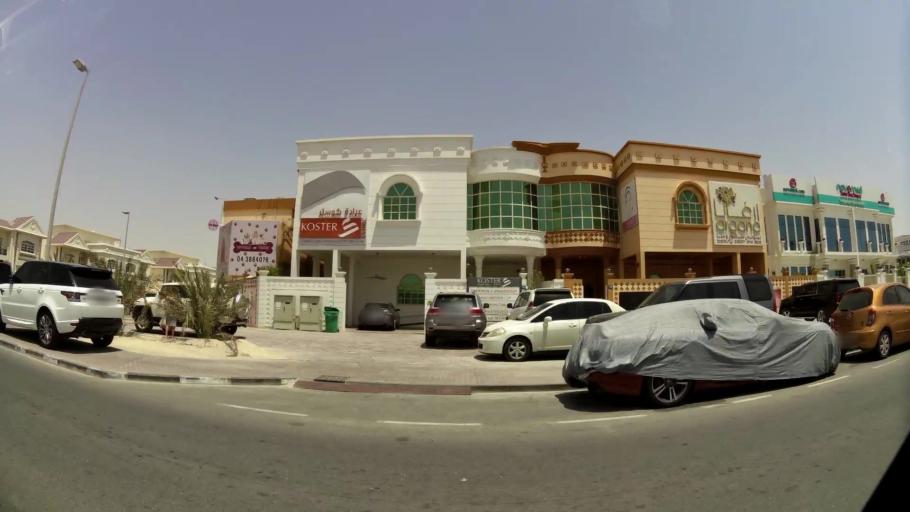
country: AE
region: Dubai
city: Dubai
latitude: 25.1355
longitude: 55.1966
